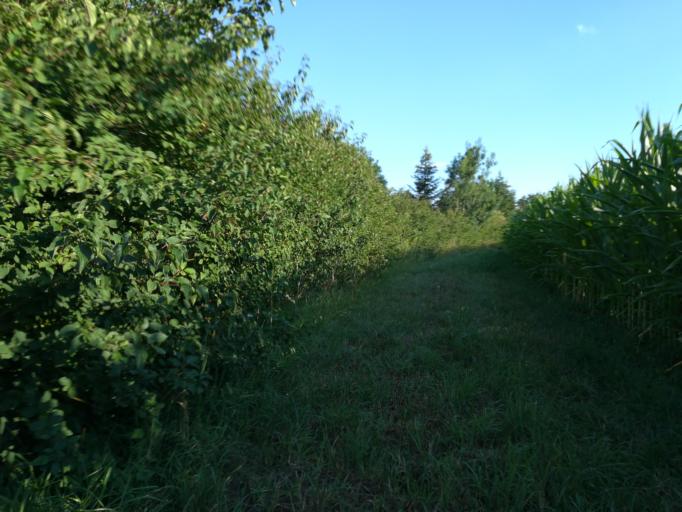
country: DE
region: Baden-Wuerttemberg
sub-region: Freiburg Region
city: Singen
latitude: 47.7548
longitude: 8.8223
